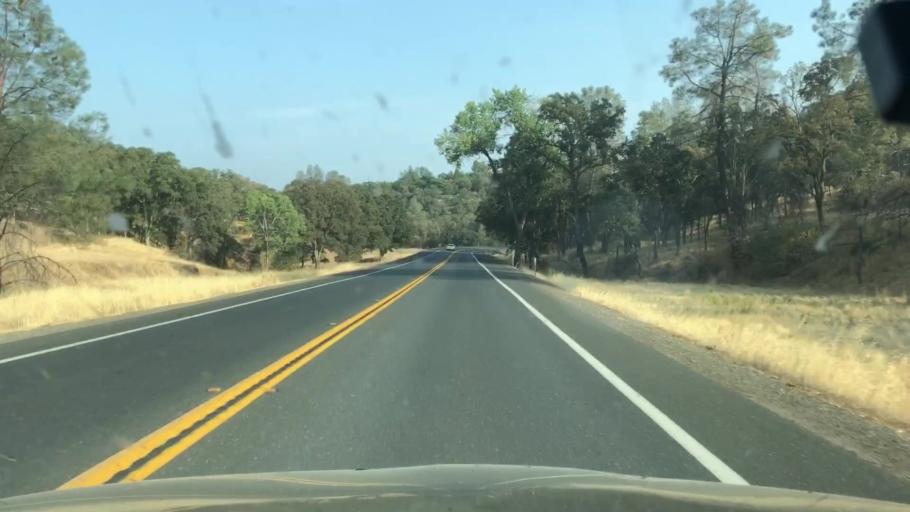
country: US
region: California
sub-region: Lake County
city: Hidden Valley Lake
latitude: 38.8171
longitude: -122.5742
